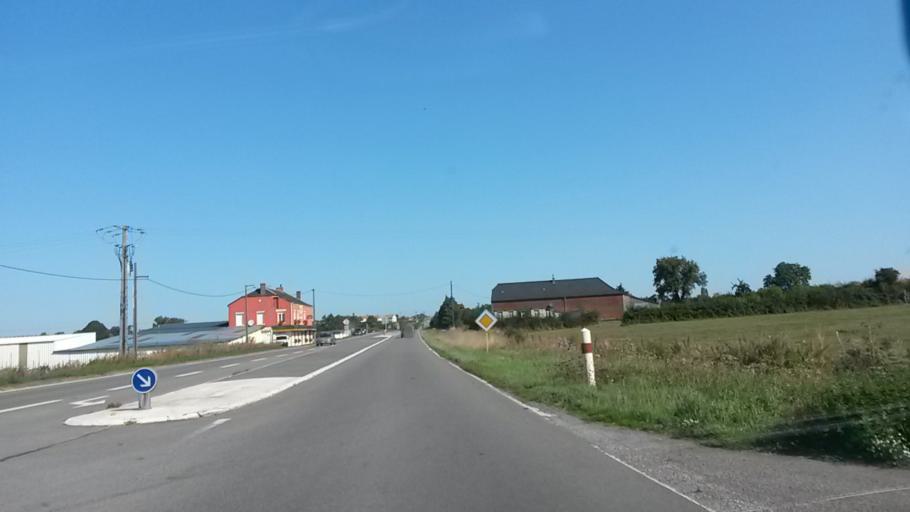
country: FR
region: Nord-Pas-de-Calais
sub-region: Departement du Nord
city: Avesnes-sur-Helpe
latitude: 50.0680
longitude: 3.9287
